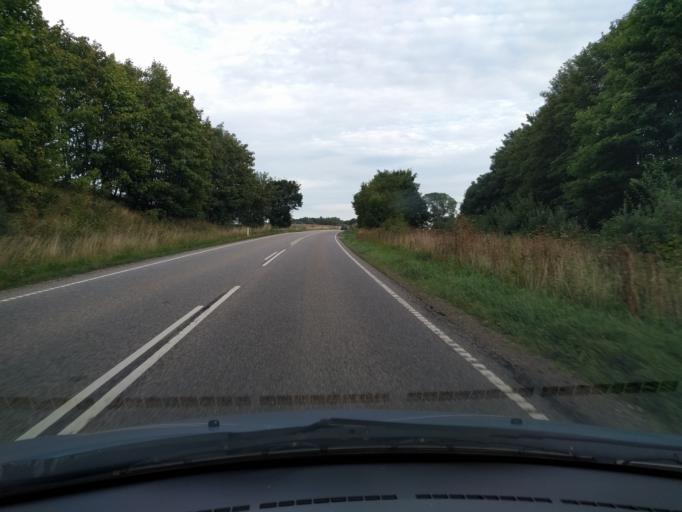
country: DK
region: Zealand
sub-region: Vordingborg Kommune
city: Nyrad
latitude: 55.0122
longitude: 11.9714
